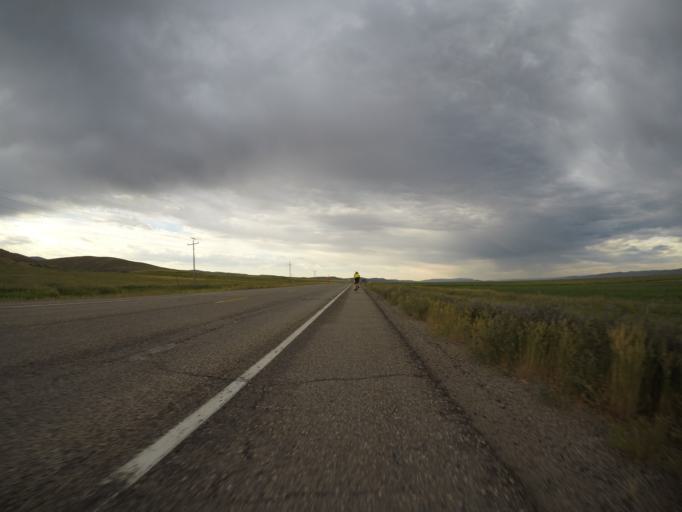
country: US
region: Utah
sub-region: Rich County
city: Randolph
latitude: 41.9612
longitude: -110.9480
